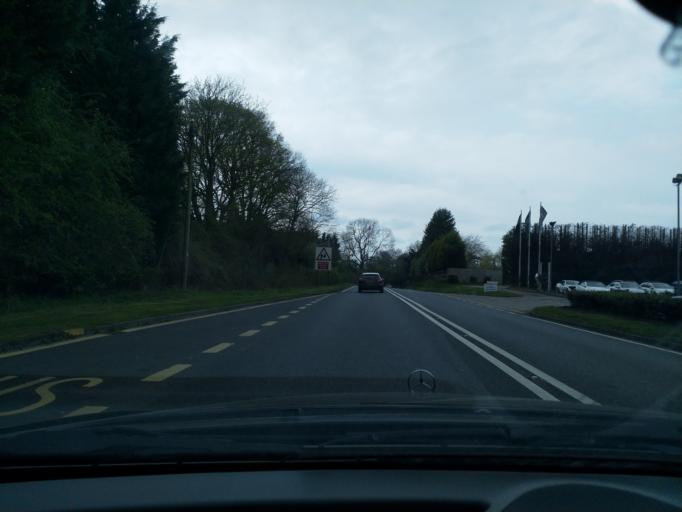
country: GB
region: England
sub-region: Warwickshire
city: Stratford-upon-Avon
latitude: 52.2310
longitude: -1.6586
